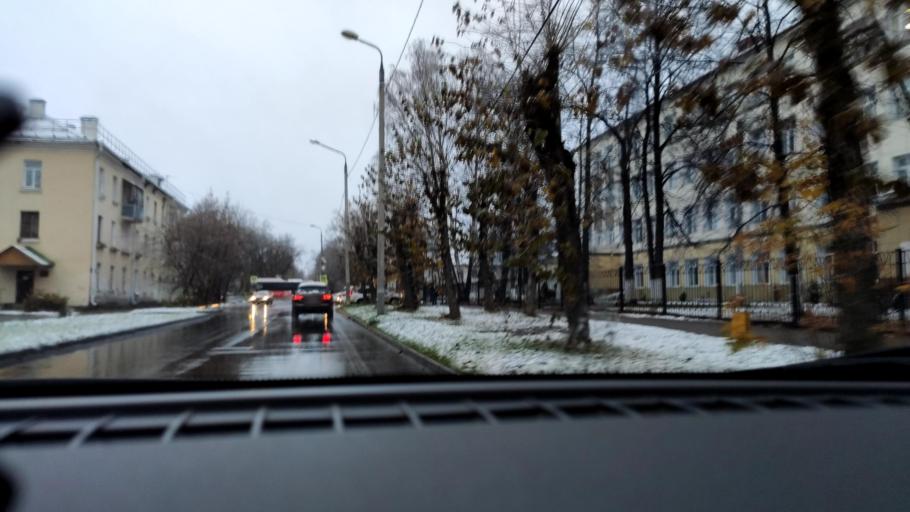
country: RU
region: Perm
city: Kultayevo
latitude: 57.9990
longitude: 55.9440
